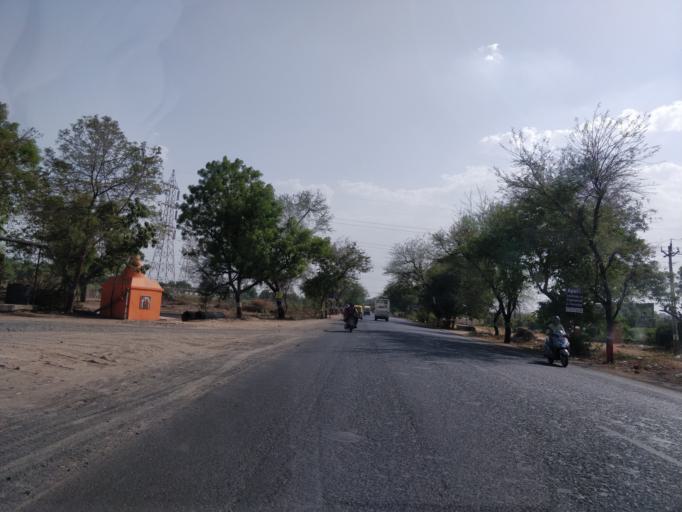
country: IN
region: Gujarat
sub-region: Ahmadabad
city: Naroda
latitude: 23.0933
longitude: 72.6936
